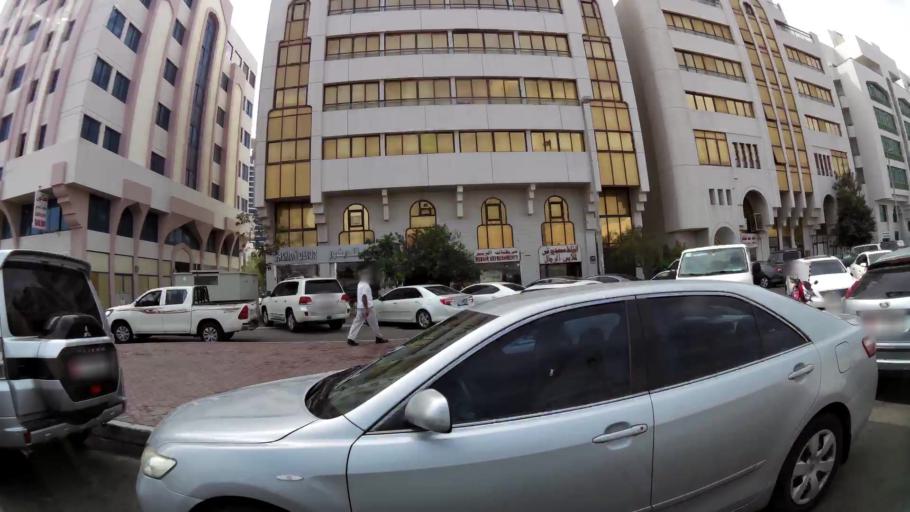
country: AE
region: Abu Dhabi
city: Abu Dhabi
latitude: 24.4349
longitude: 54.4328
